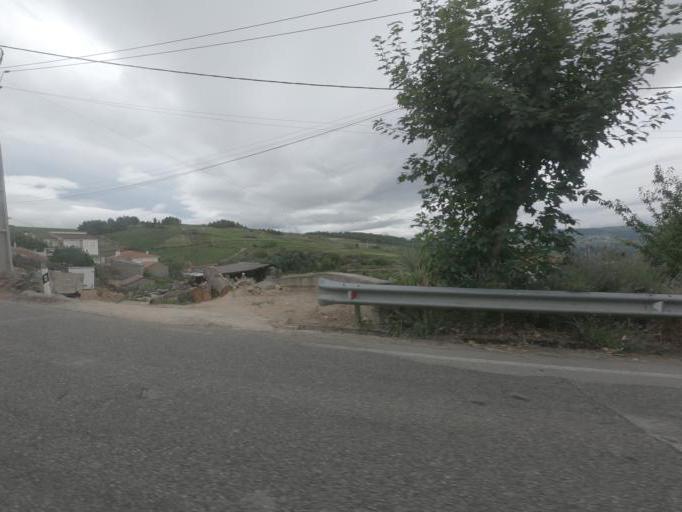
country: PT
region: Vila Real
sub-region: Sabrosa
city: Sabrosa
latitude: 41.2891
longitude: -7.5181
